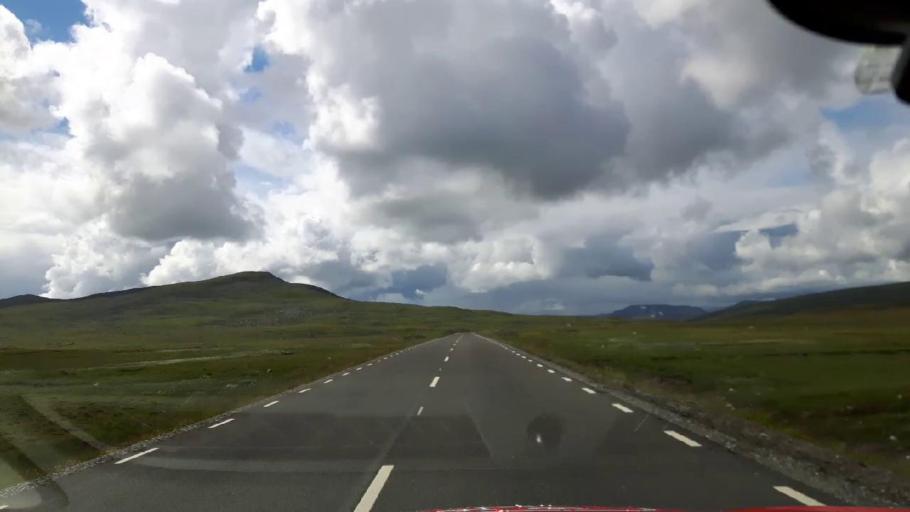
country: NO
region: Nordland
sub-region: Hattfjelldal
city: Hattfjelldal
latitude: 65.0621
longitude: 14.3771
